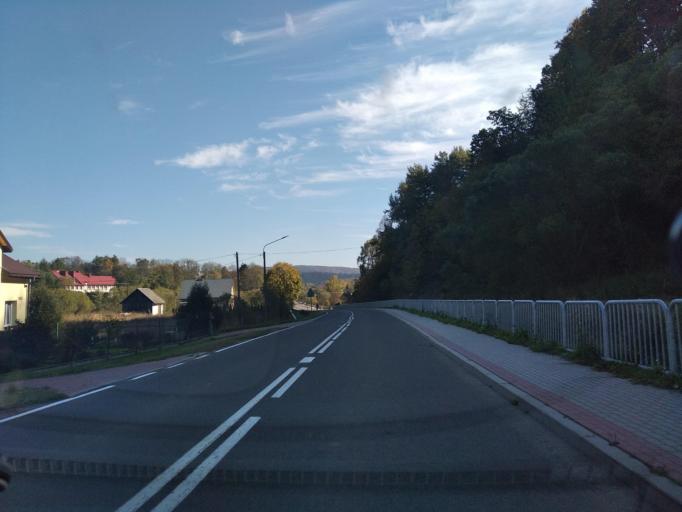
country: PL
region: Subcarpathian Voivodeship
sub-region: Powiat sanocki
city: Komancza
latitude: 49.3405
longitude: 22.0491
